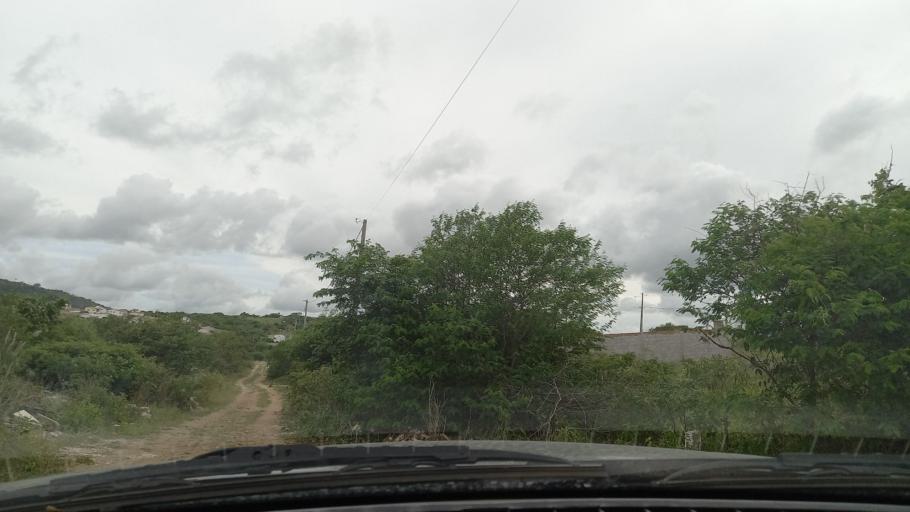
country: BR
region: Pernambuco
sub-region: Gravata
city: Gravata
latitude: -8.2253
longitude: -35.5740
